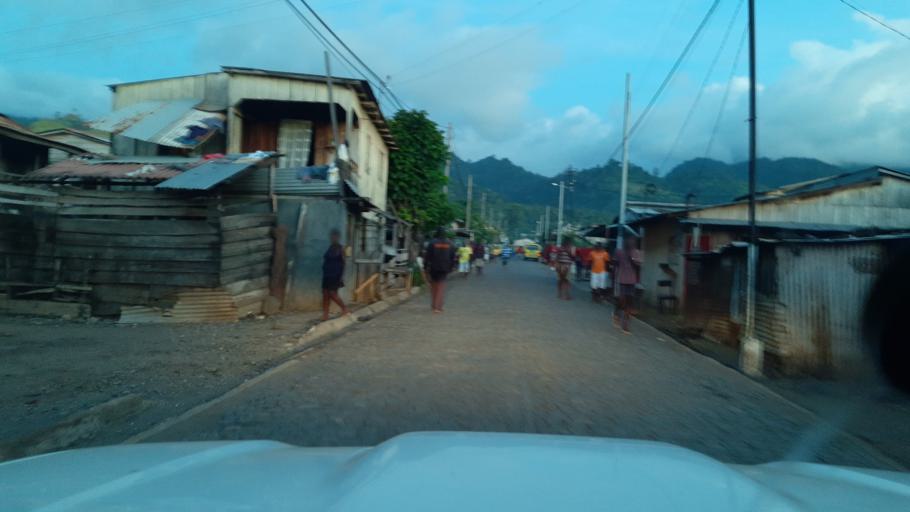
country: ST
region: Sao Tome Island
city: Sao Tome
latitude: 0.3595
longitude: 6.5476
